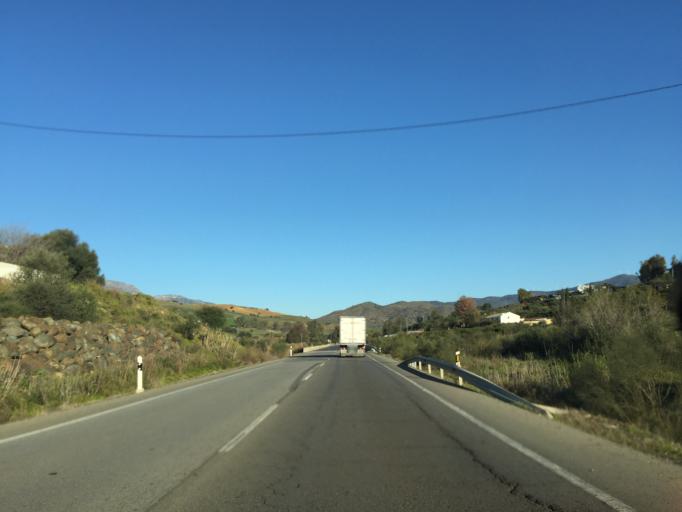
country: ES
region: Andalusia
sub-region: Provincia de Malaga
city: Pizarra
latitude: 36.7883
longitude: -4.7472
